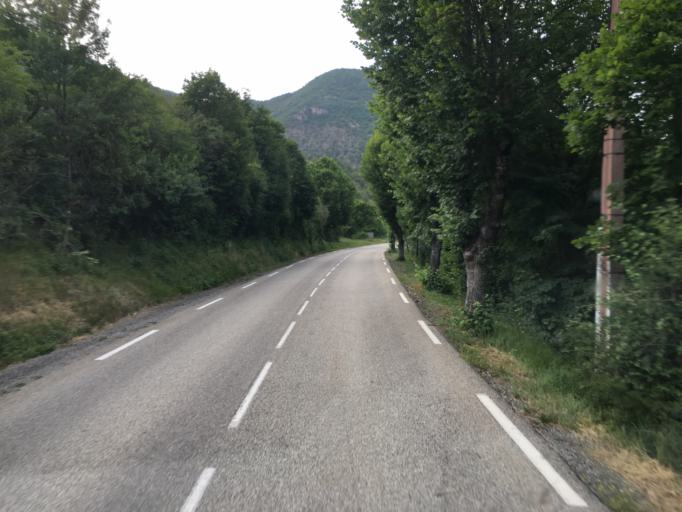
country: FR
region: Rhone-Alpes
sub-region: Departement de la Drome
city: Buis-les-Baronnies
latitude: 44.3956
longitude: 5.3527
